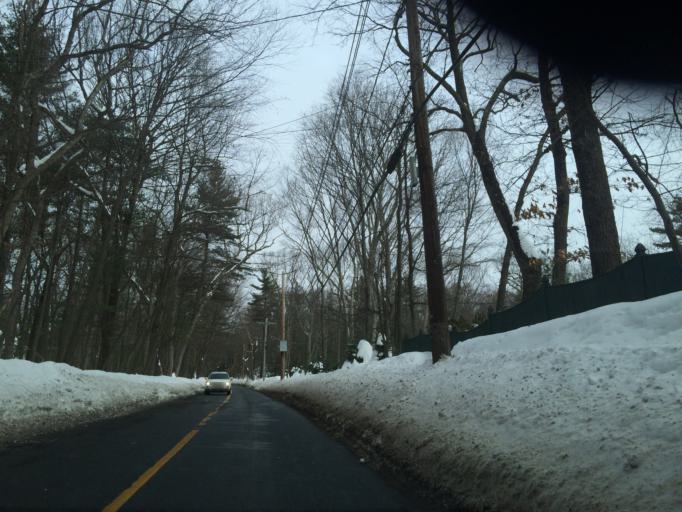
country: US
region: Massachusetts
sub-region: Middlesex County
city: Weston
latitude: 42.3463
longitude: -71.3203
